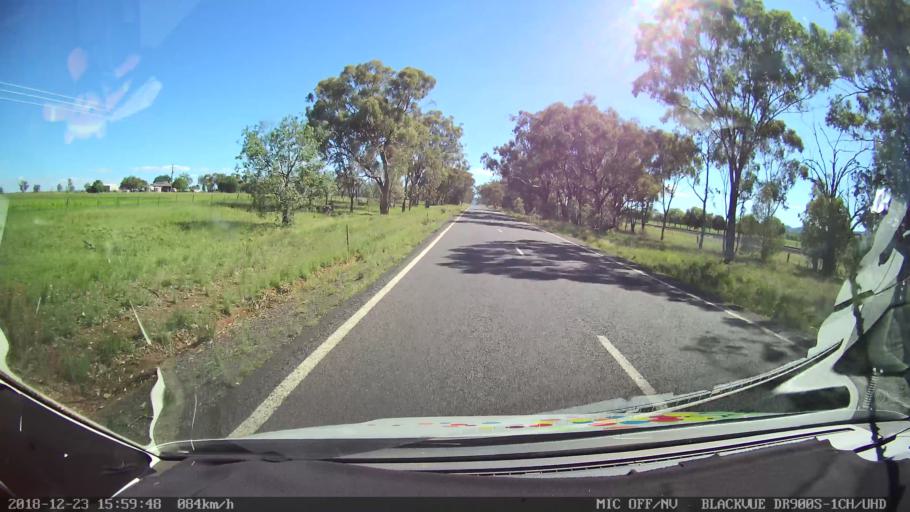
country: AU
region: New South Wales
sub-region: Tamworth Municipality
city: Phillip
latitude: -31.2038
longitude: 150.8302
